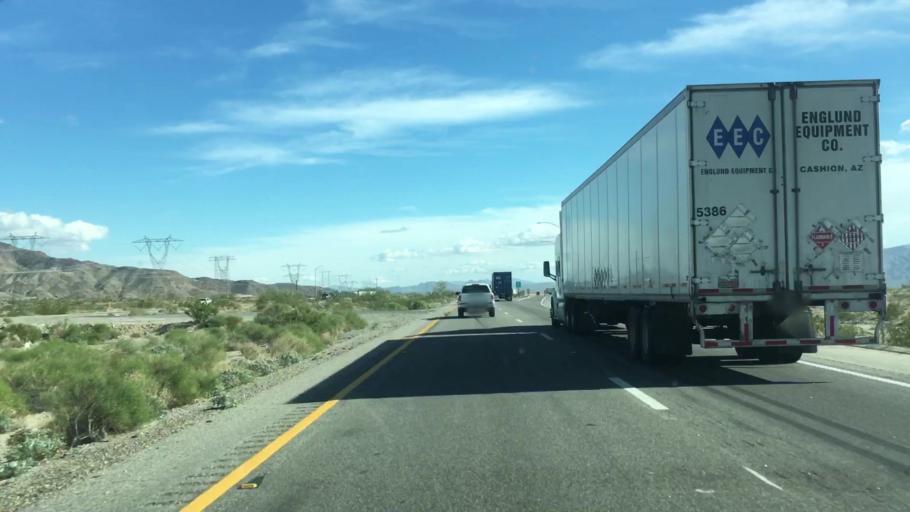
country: US
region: California
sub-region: Riverside County
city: Mecca
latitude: 33.6793
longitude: -115.9704
